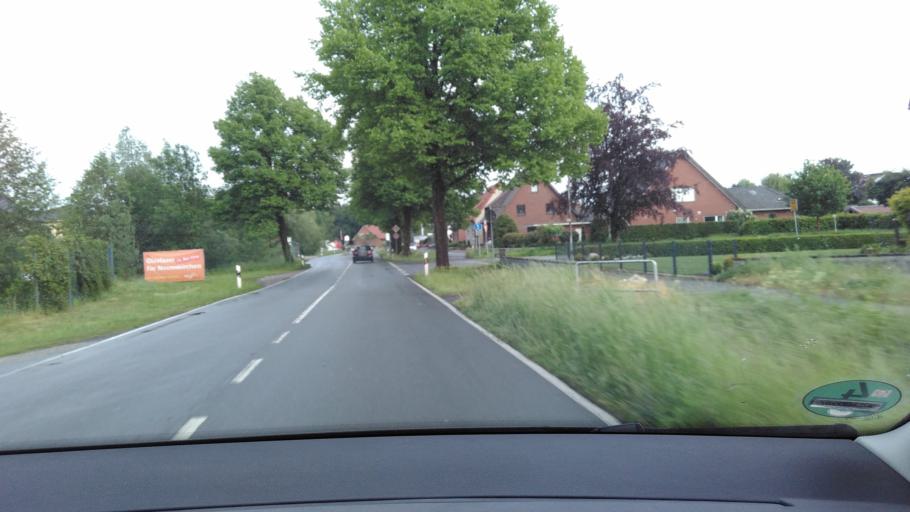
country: DE
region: North Rhine-Westphalia
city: Rietberg
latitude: 51.8404
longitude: 8.4438
